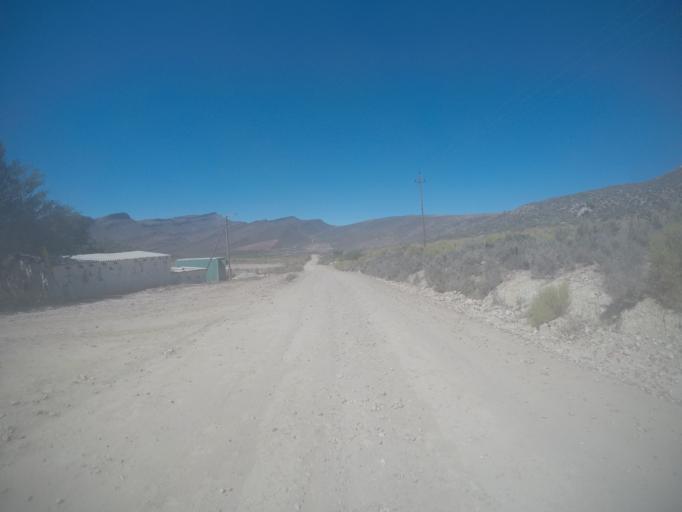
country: ZA
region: Western Cape
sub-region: West Coast District Municipality
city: Clanwilliam
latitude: -32.5515
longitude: 19.3609
